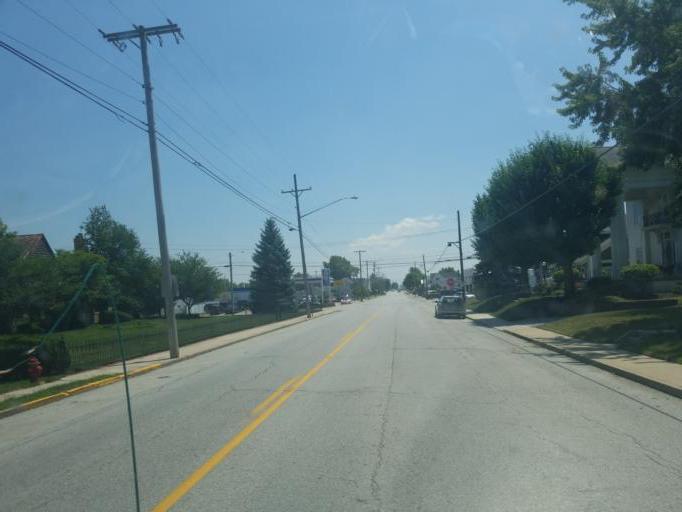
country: US
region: Ohio
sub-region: Shelby County
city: Botkins
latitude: 40.4685
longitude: -84.1822
